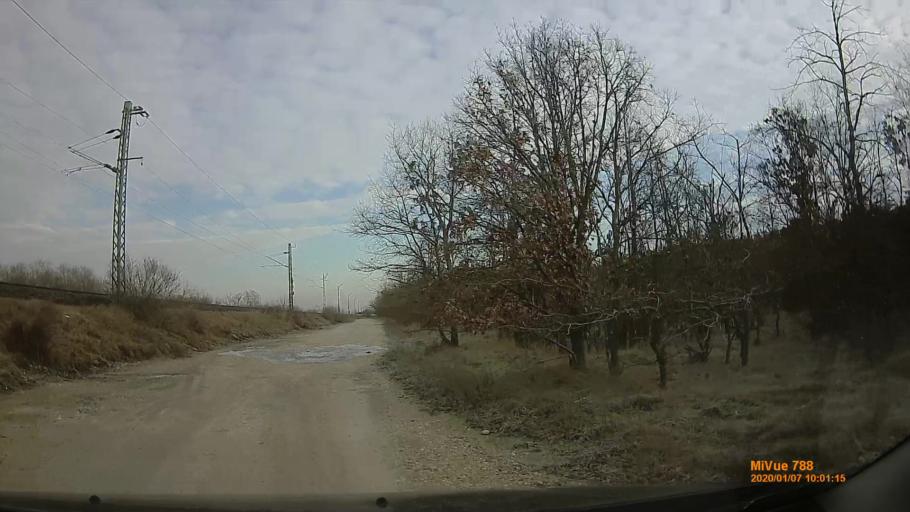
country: HU
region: Gyor-Moson-Sopron
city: Rajka
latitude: 47.9359
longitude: 17.1691
